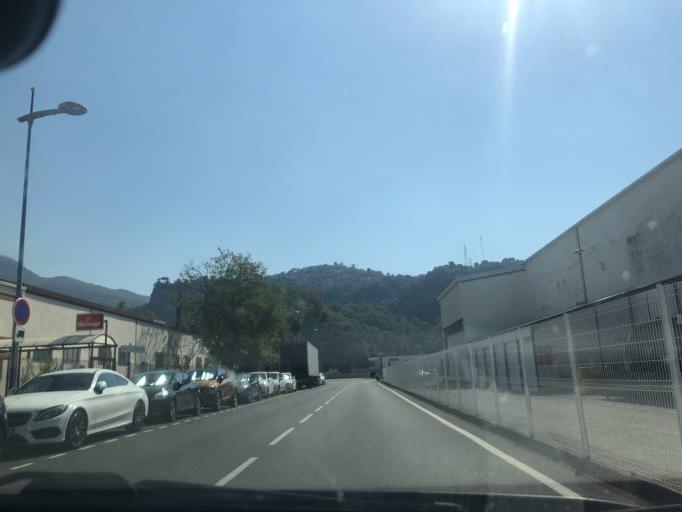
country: FR
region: Provence-Alpes-Cote d'Azur
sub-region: Departement des Alpes-Maritimes
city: Colomars
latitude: 43.7728
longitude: 7.2079
